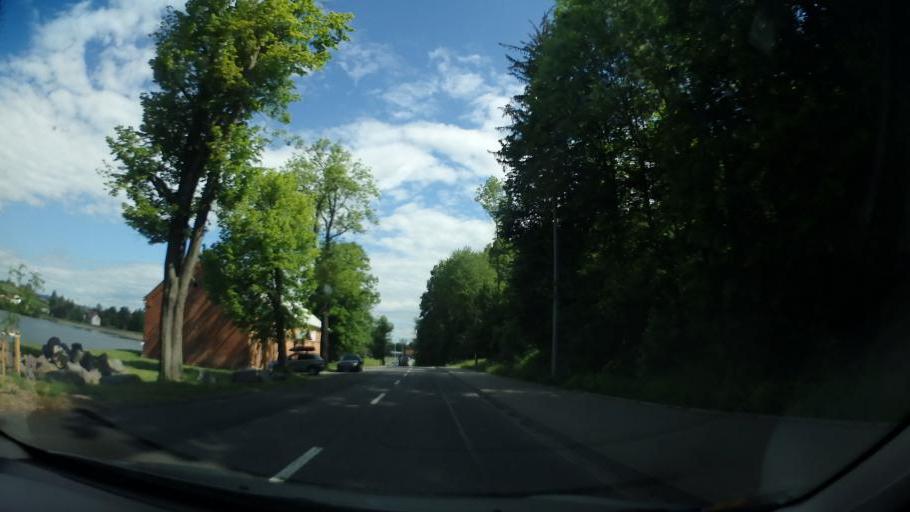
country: CZ
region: Pardubicky
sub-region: Okres Svitavy
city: Moravska Trebova
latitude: 49.7476
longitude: 16.6566
